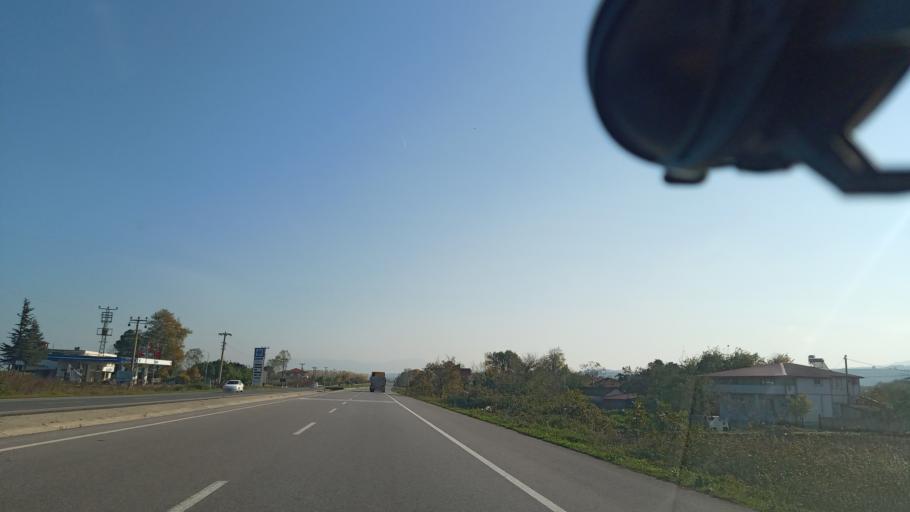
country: TR
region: Sakarya
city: Karasu
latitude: 41.0769
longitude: 30.7791
